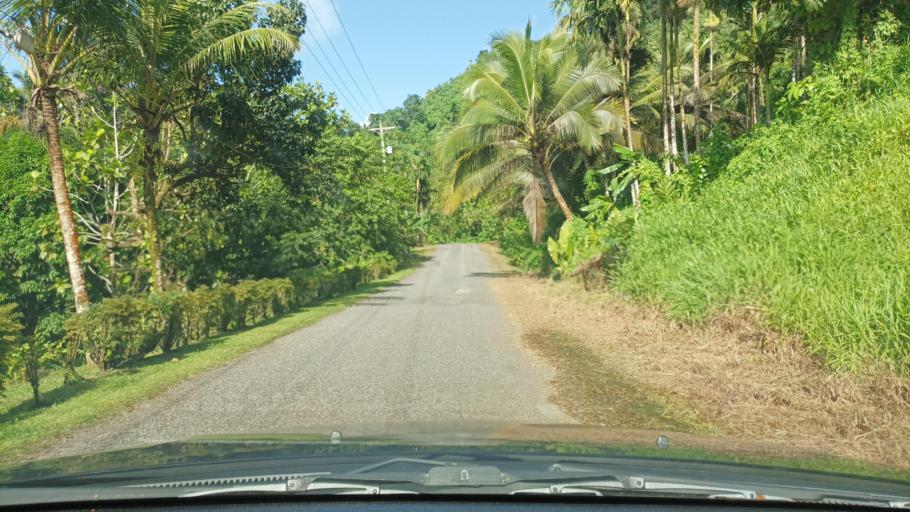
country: FM
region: Kosrae
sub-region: Tafunsak Municipality
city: Tafunsak
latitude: 5.3641
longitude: 162.9913
